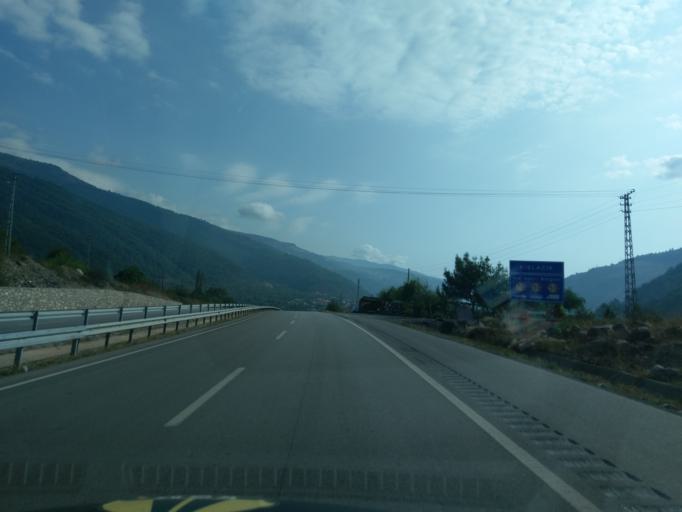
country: TR
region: Amasya
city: Akdag
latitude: 40.7471
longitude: 36.0400
